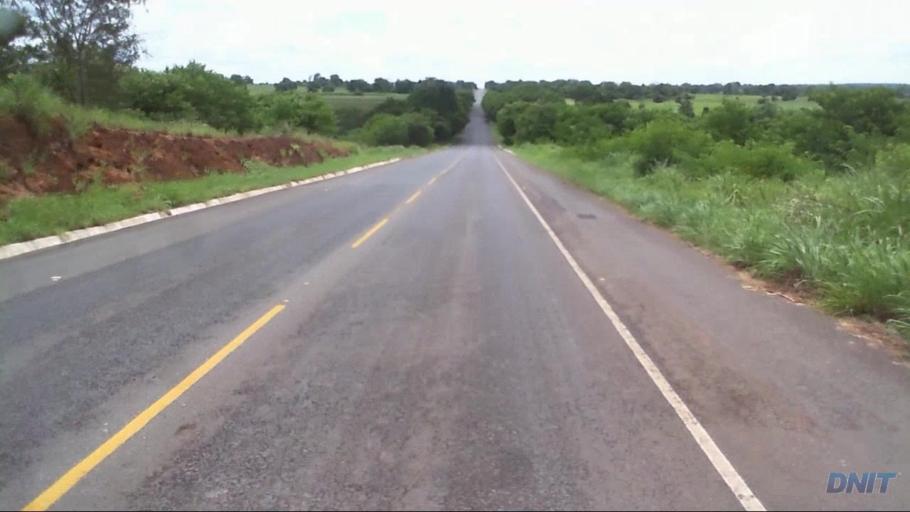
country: BR
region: Goias
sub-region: Sao Miguel Do Araguaia
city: Sao Miguel do Araguaia
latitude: -13.2867
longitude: -50.1942
